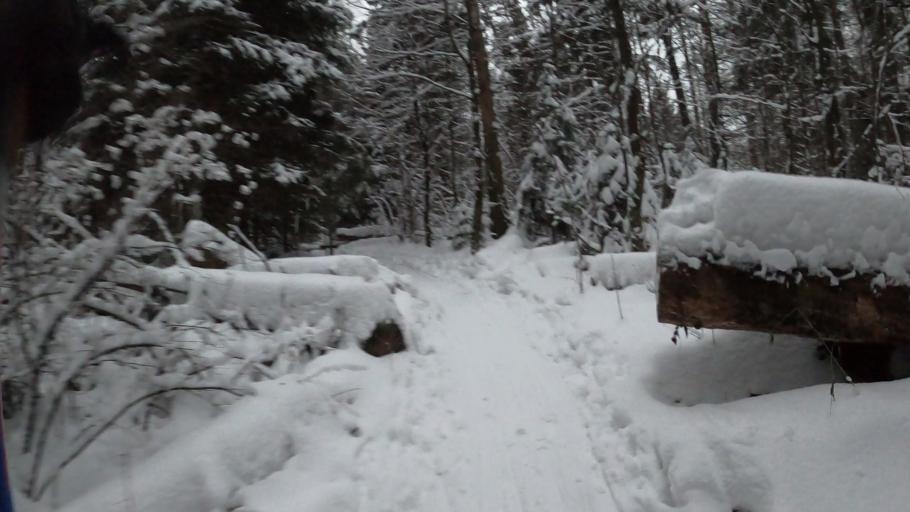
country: RU
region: Moskovskaya
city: Nakhabino
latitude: 55.8942
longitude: 37.2080
